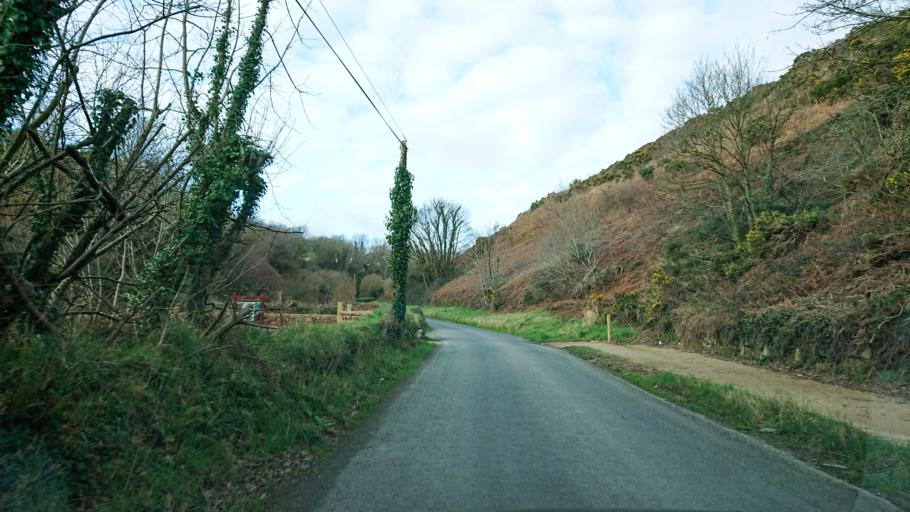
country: IE
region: Munster
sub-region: Waterford
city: Tra Mhor
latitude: 52.1563
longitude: -7.2651
